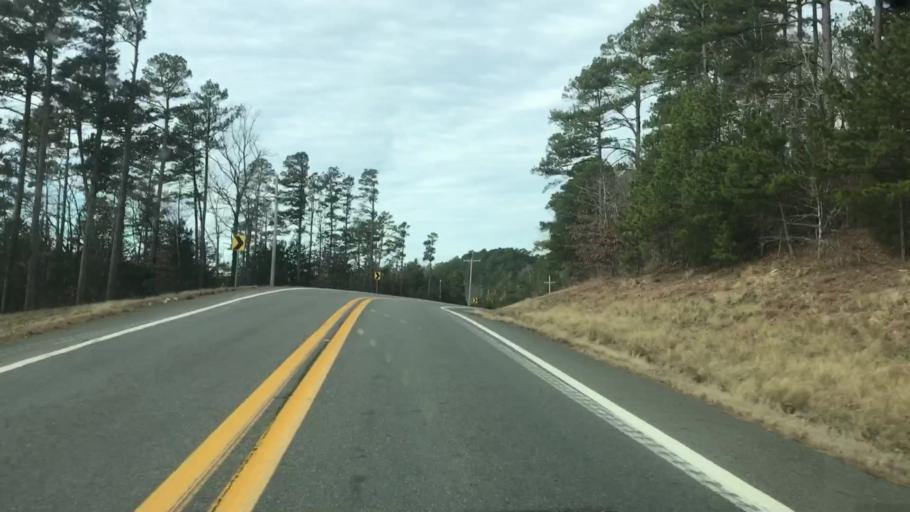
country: US
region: Arkansas
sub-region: Montgomery County
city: Mount Ida
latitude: 34.6198
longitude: -93.7060
